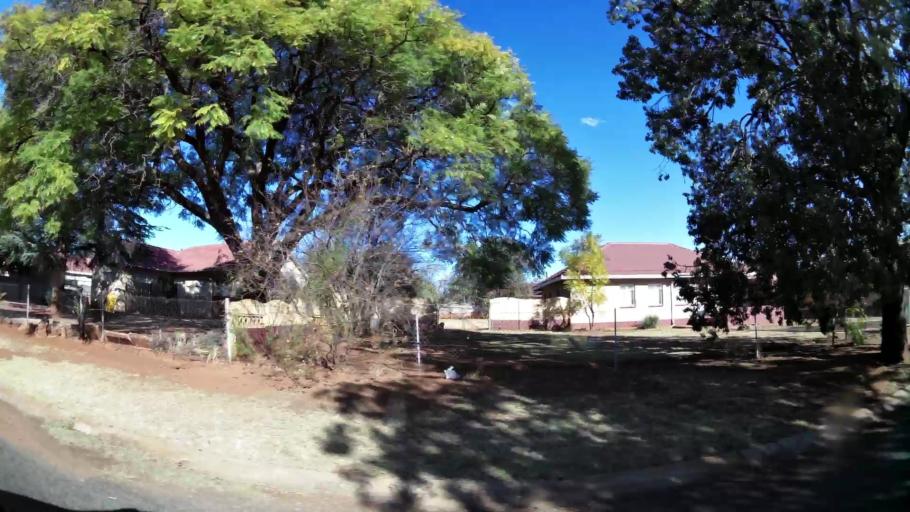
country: ZA
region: Gauteng
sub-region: West Rand District Municipality
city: Carletonville
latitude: -26.3716
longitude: 27.4035
